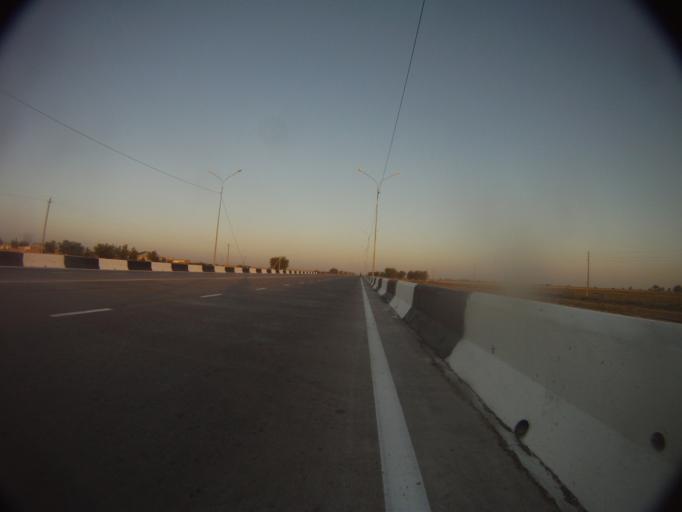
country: KZ
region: Ongtustik Qazaqstan
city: Turkestan
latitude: 43.2527
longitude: 68.3926
